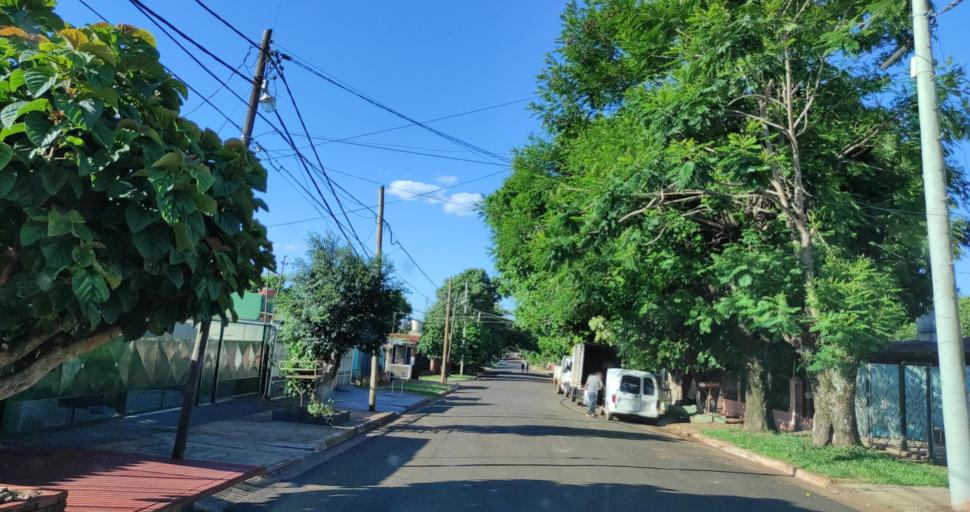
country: AR
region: Misiones
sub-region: Departamento de Capital
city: Posadas
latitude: -27.3769
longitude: -55.9312
